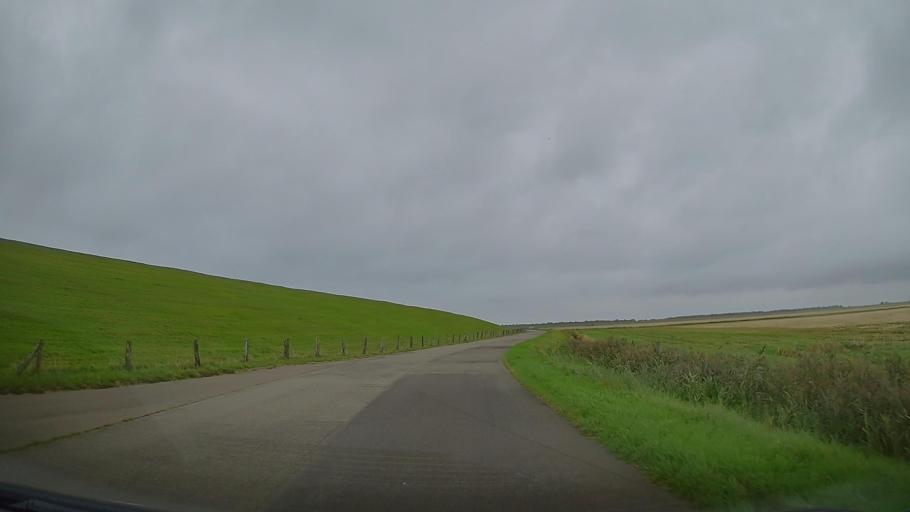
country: DE
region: Schleswig-Holstein
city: Busenwurth
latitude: 54.0603
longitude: 8.9872
